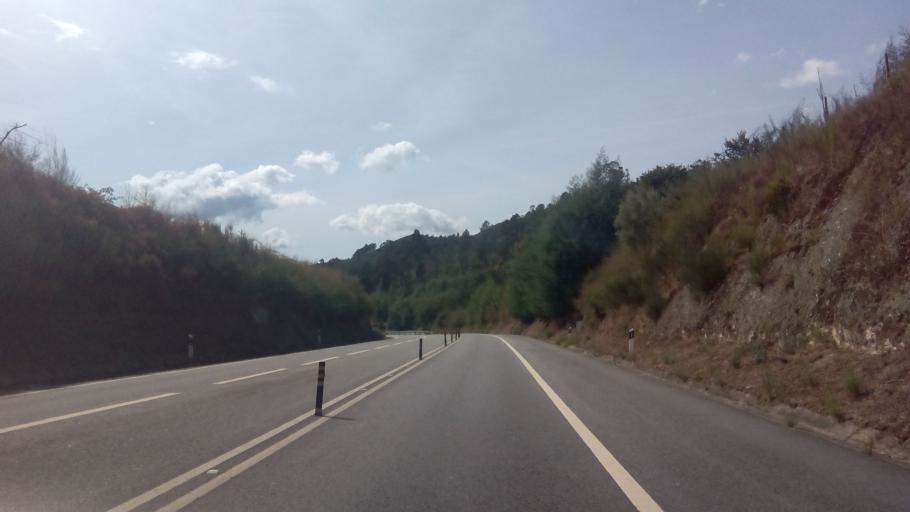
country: PT
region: Porto
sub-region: Amarante
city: Amarante
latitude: 41.2722
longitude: -8.0120
